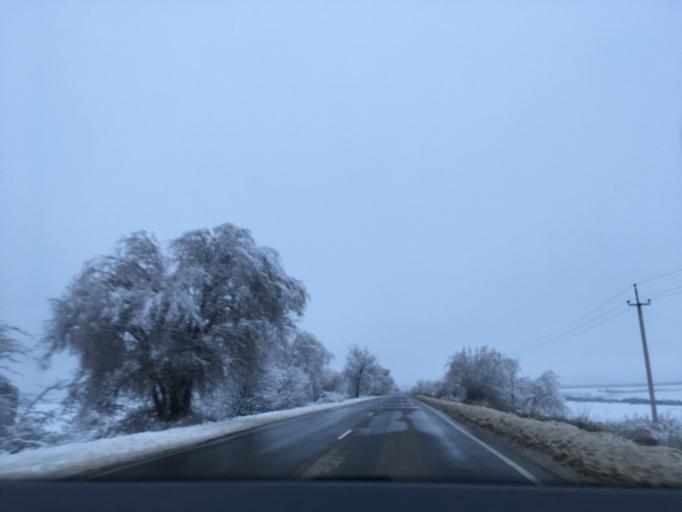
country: RU
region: Voronezj
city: Verkhniy Mamon
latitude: 50.0208
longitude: 40.1050
